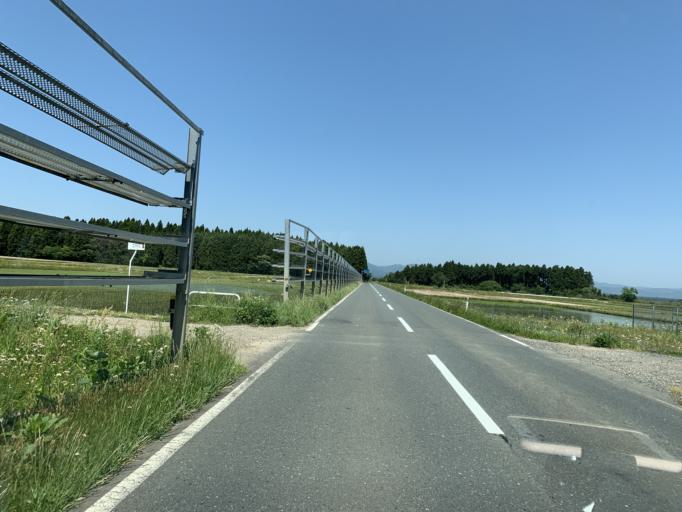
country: JP
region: Iwate
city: Kitakami
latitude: 39.2733
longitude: 141.0531
